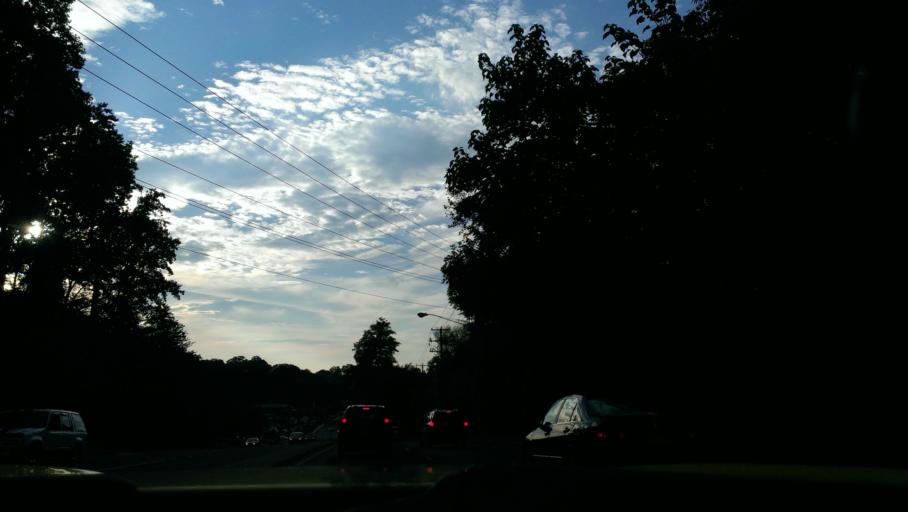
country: US
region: Virginia
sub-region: Fairfax County
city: Pimmit Hills
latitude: 38.9010
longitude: -77.2001
